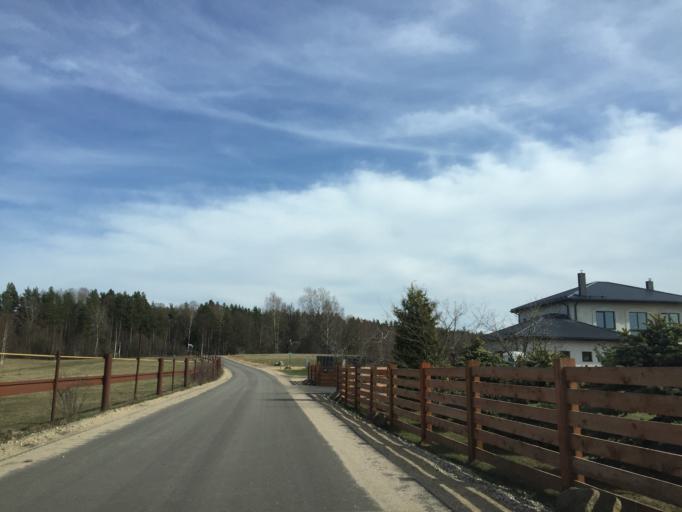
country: LV
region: Ikskile
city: Ikskile
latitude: 56.8422
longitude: 24.5289
